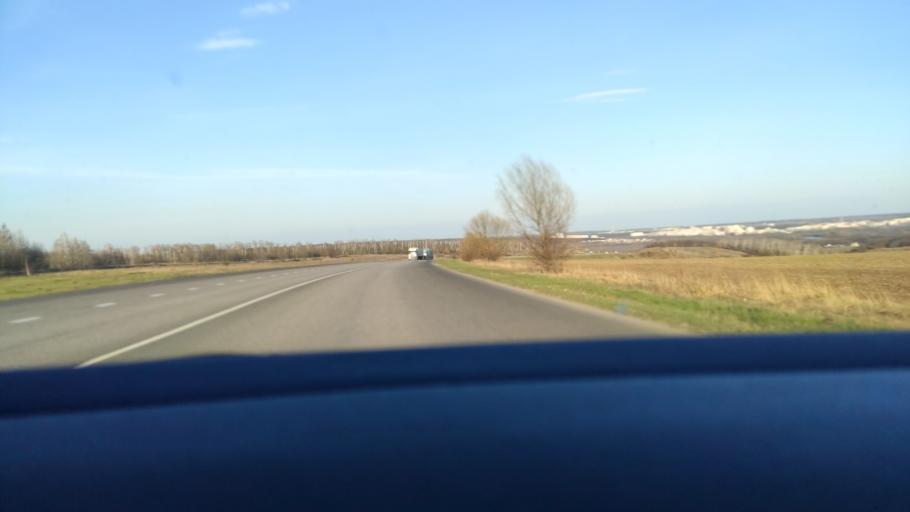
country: RU
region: Voronezj
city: Kolodeznyy
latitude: 51.3285
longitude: 39.1334
